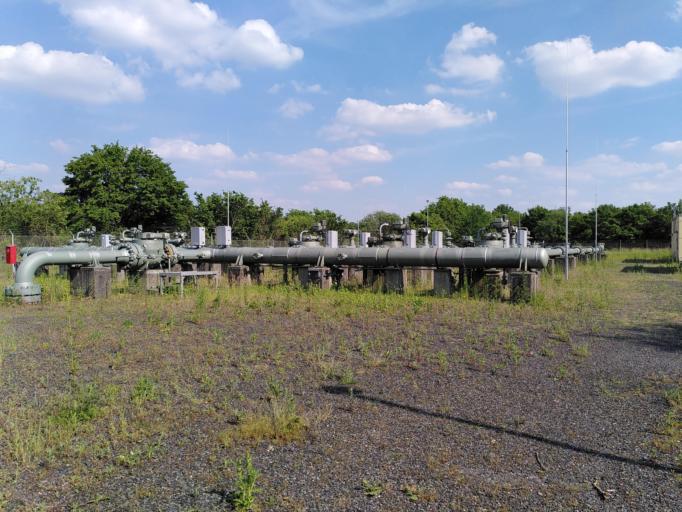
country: DE
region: North Rhine-Westphalia
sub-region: Regierungsbezirk Munster
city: Gronau
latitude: 52.1701
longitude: 6.9921
